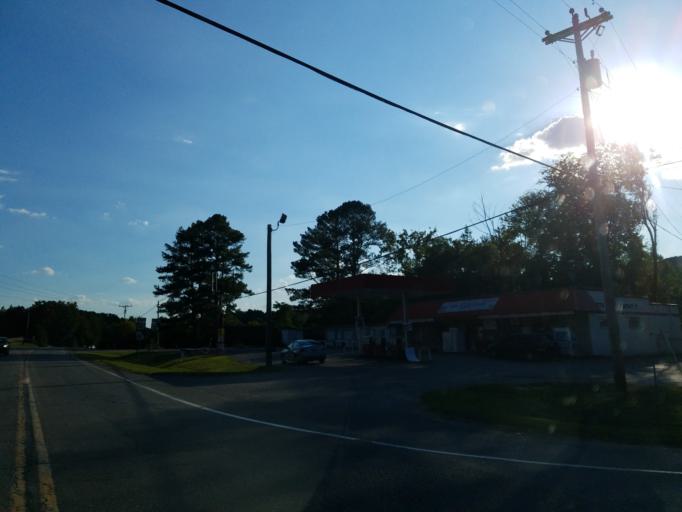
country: US
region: Tennessee
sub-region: Bradley County
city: Wildwood Lake
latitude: 34.9512
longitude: -84.7371
